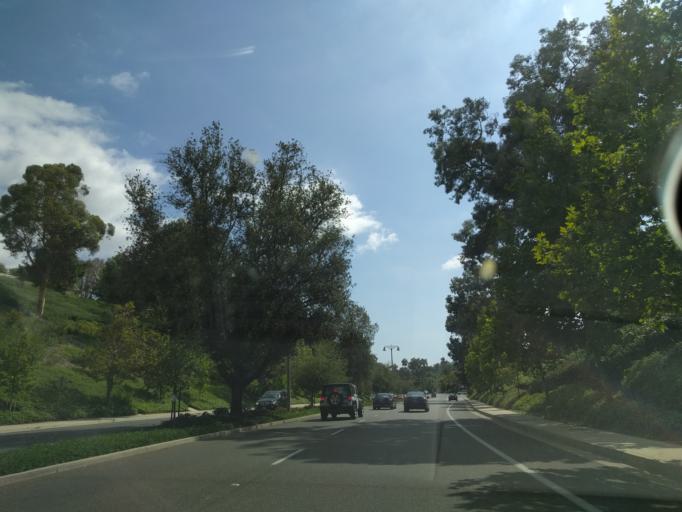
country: US
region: California
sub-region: Orange County
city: Mission Viejo
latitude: 33.6093
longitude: -117.6544
